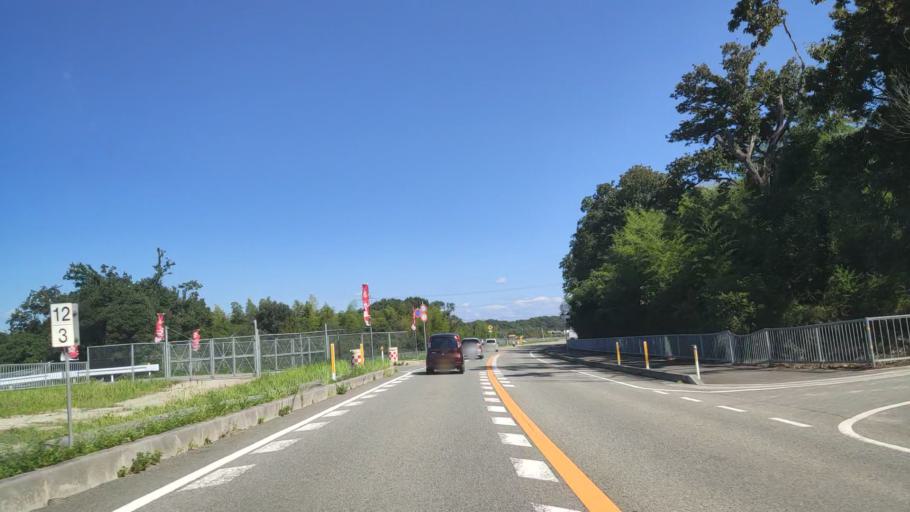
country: JP
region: Hyogo
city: Miki
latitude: 34.7599
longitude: 134.9759
